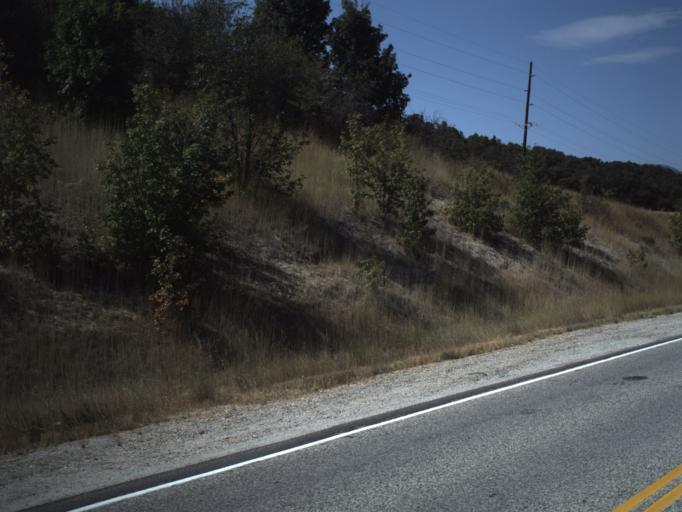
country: US
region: Utah
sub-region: Weber County
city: Wolf Creek
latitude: 41.2895
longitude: -111.8255
